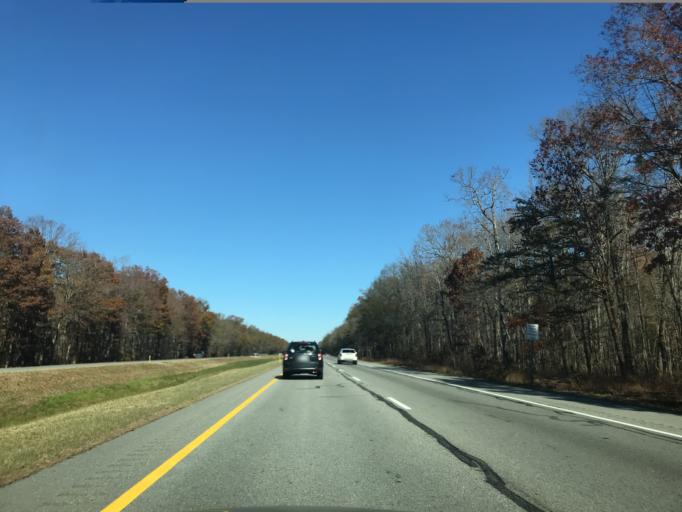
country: US
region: Delaware
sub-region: New Castle County
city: Townsend
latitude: 39.3012
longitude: -75.8513
